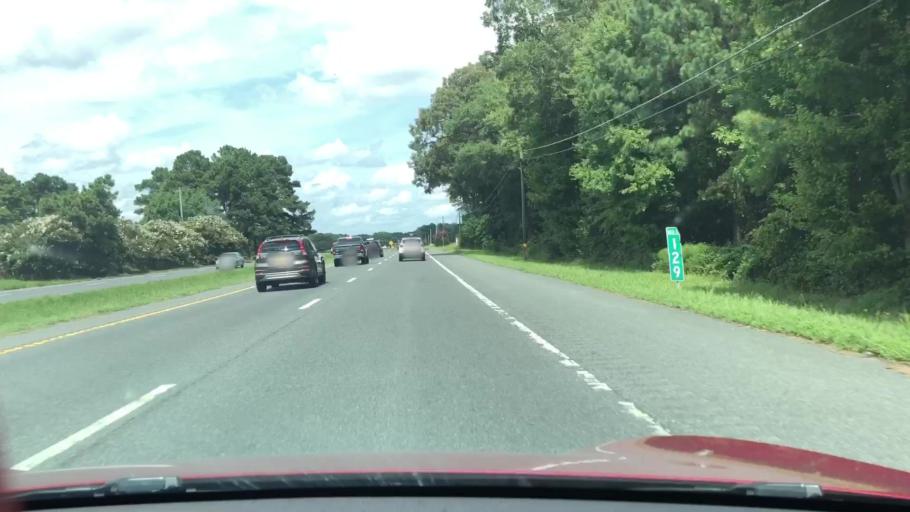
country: US
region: Virginia
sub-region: Accomack County
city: Wattsville
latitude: 37.8802
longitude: -75.5571
